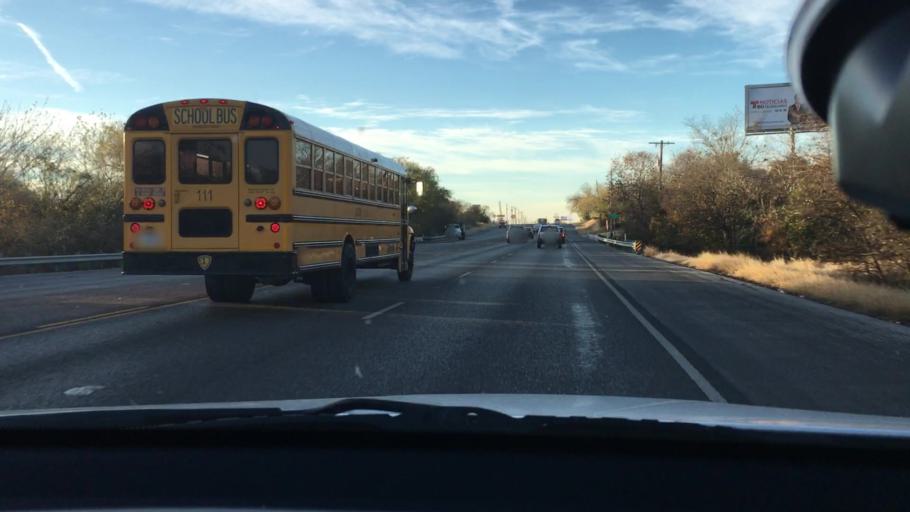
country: US
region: Texas
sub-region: Bexar County
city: Converse
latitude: 29.5209
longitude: -98.3081
